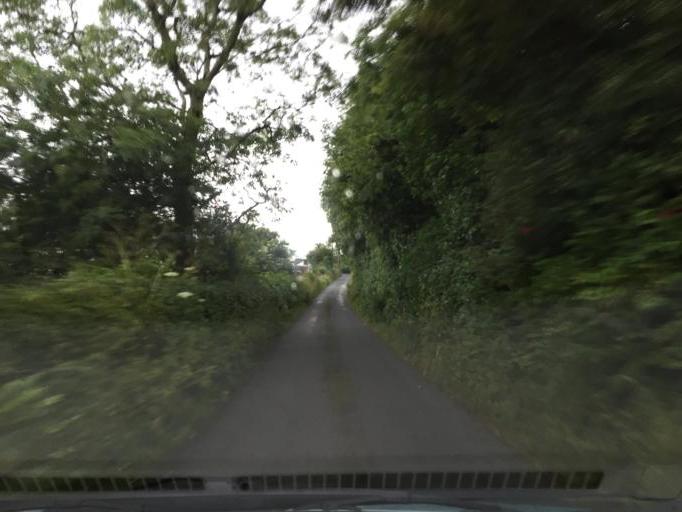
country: IE
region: Connaught
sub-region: Sligo
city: Strandhill
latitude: 54.2488
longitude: -8.5663
